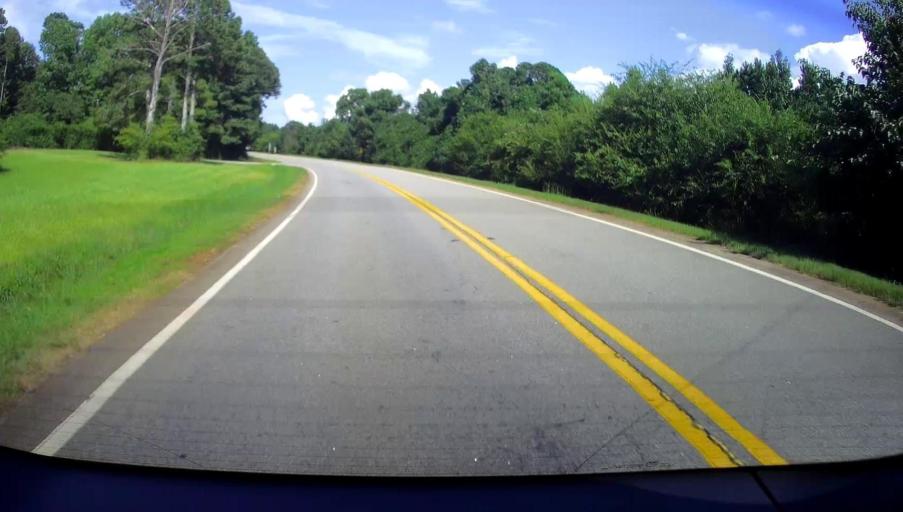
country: US
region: Georgia
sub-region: Upson County
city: Thomaston
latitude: 32.8959
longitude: -84.3479
